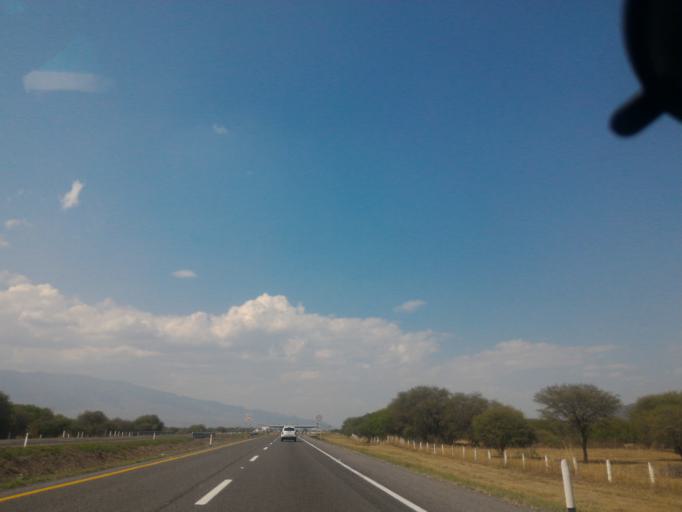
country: MX
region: Jalisco
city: Usmajac
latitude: 19.9245
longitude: -103.5287
